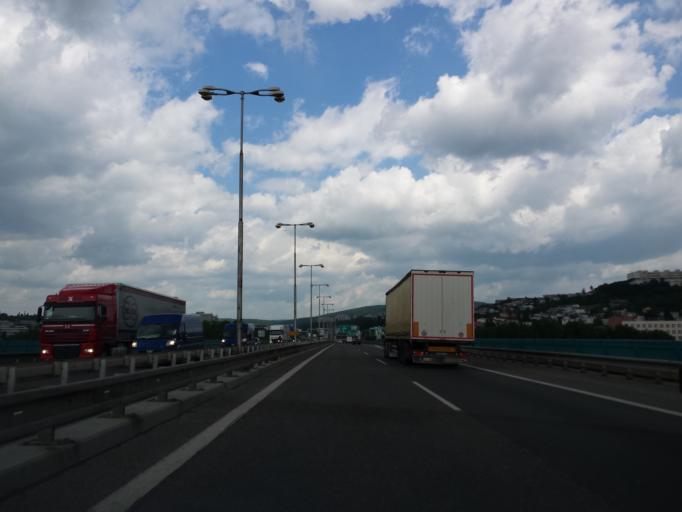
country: SK
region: Bratislavsky
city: Bratislava
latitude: 48.1411
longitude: 17.0753
